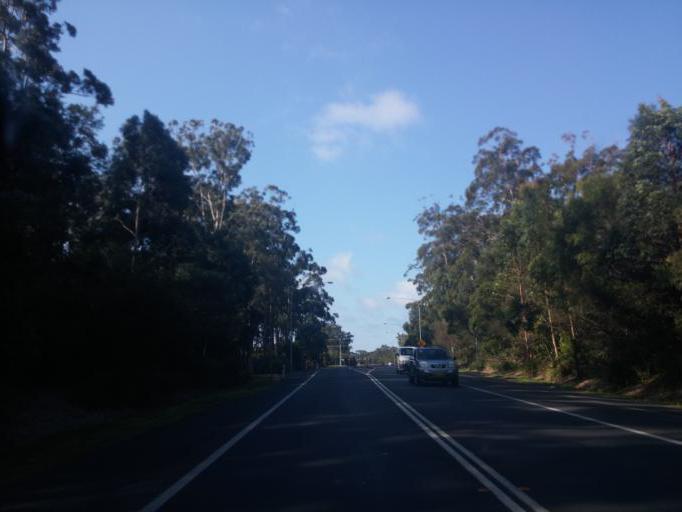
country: AU
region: New South Wales
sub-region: Coffs Harbour
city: Coffs Harbour
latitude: -30.2970
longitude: 153.1287
